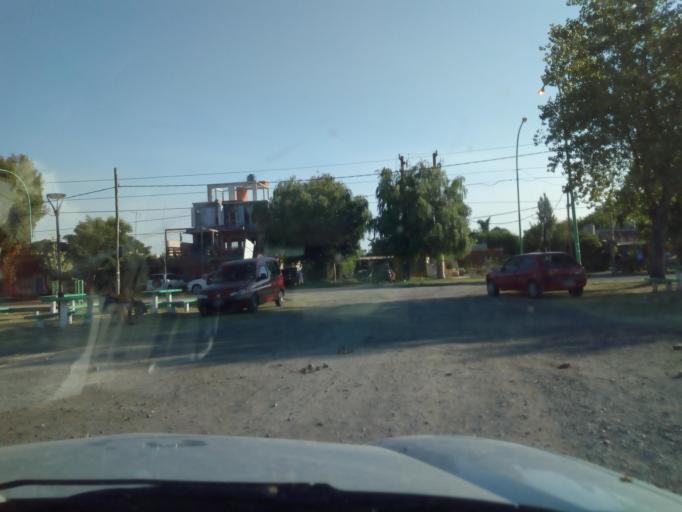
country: AR
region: Buenos Aires
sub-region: Partido de Ensenada
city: Ensenada
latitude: -34.8252
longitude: -57.9605
